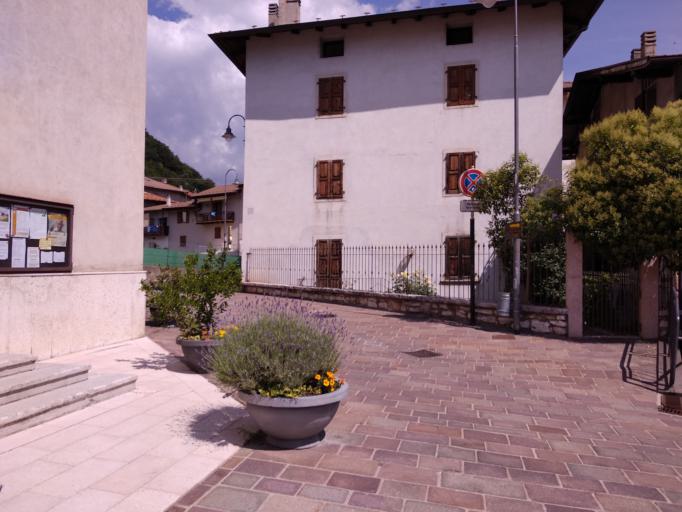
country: IT
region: Trentino-Alto Adige
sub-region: Provincia di Trento
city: Trento
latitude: 46.0634
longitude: 11.0970
